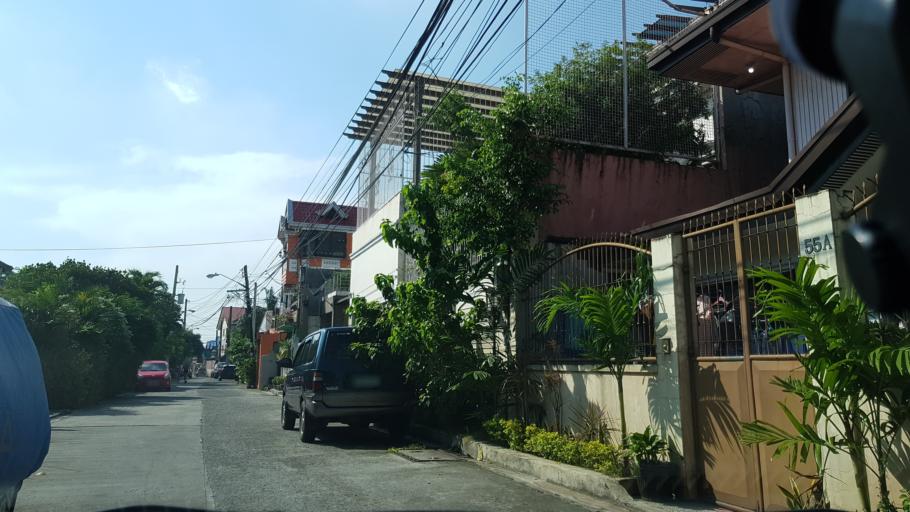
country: PH
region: Metro Manila
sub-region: Quezon City
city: Quezon City
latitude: 14.6248
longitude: 121.0447
